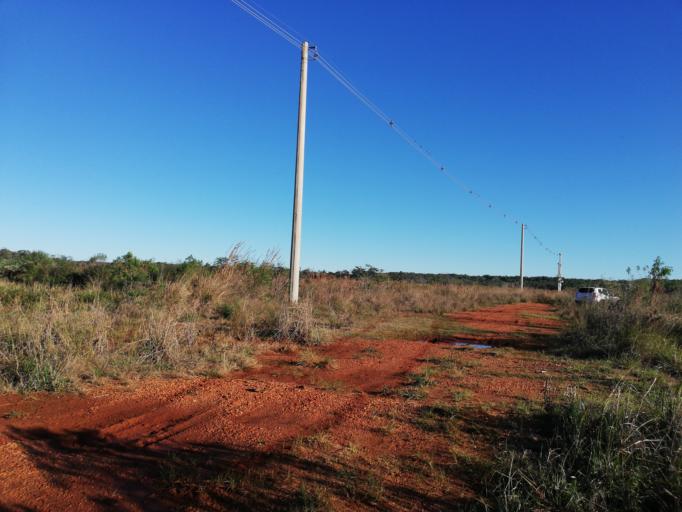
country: AR
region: Misiones
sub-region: Departamento de Candelaria
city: Candelaria
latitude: -27.4965
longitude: -55.7720
